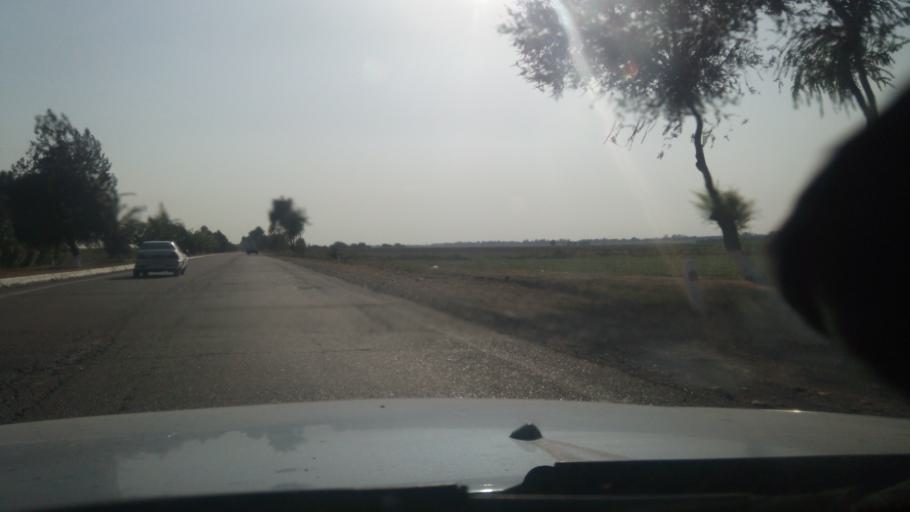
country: UZ
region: Toshkent
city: Zafar
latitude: 41.0061
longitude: 68.8305
